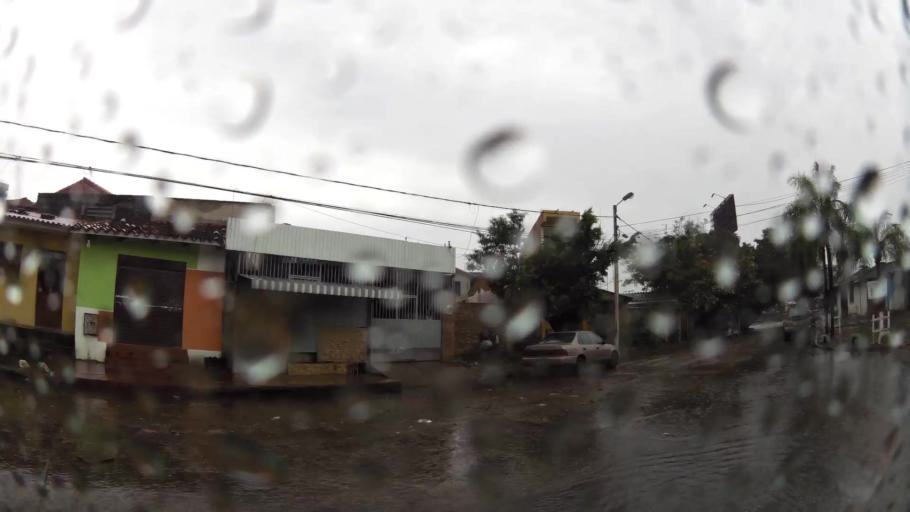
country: BO
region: Santa Cruz
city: Santa Cruz de la Sierra
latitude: -17.7830
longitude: -63.1956
